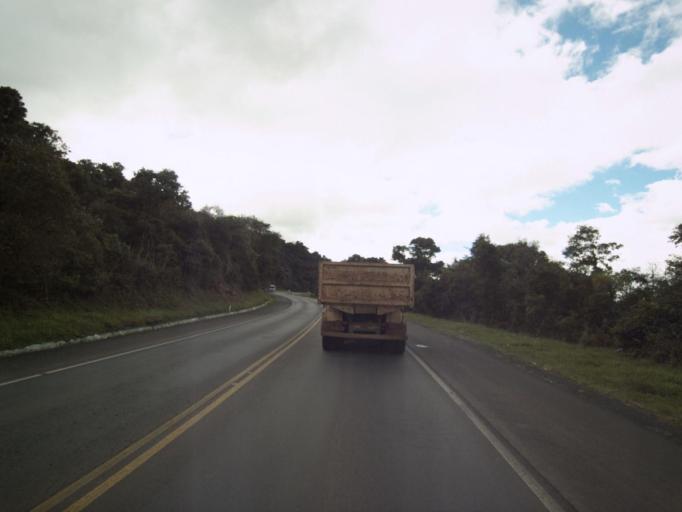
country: BR
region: Santa Catarina
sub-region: Concordia
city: Concordia
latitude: -27.2006
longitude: -51.9403
